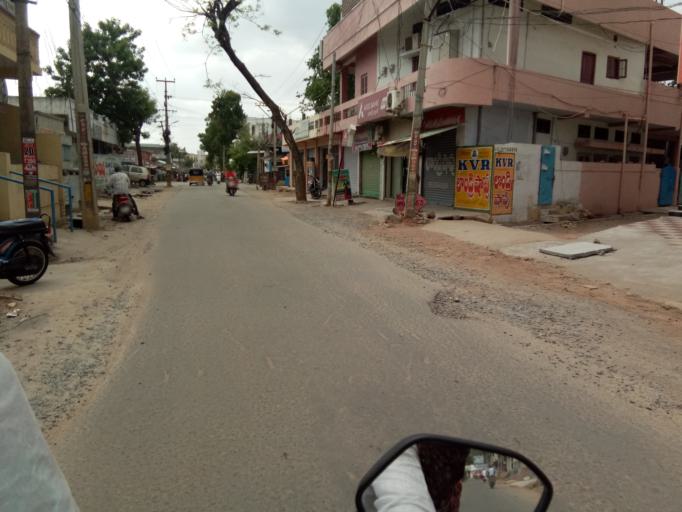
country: IN
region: Telangana
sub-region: Khammam
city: Khammam
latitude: 17.2387
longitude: 80.1449
